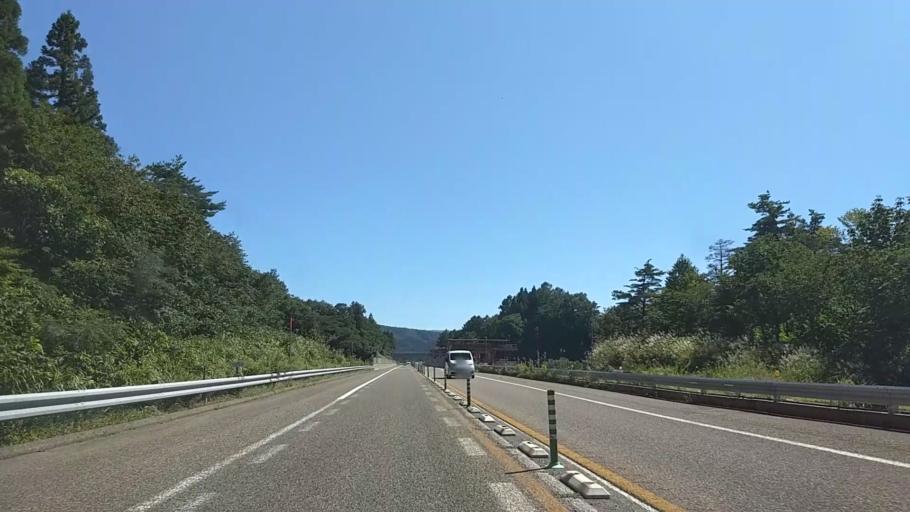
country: JP
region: Niigata
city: Arai
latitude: 36.9873
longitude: 138.2125
